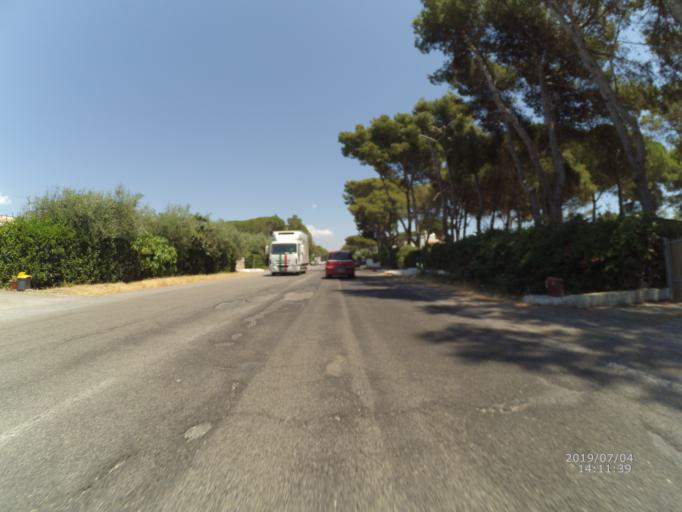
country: IT
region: Latium
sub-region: Provincia di Latina
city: Monte San Biagio
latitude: 41.2982
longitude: 13.2926
